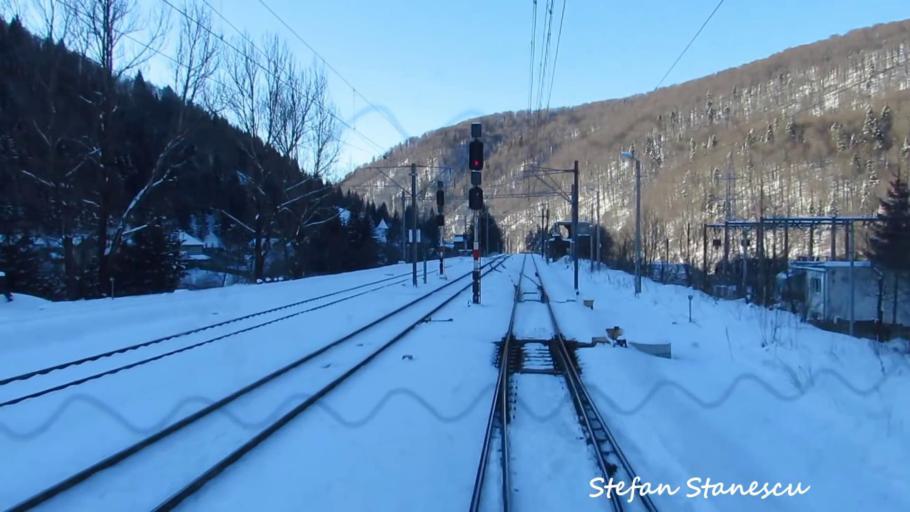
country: RO
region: Prahova
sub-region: Oras Azuga
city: Azuga
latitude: 45.4359
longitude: 25.5508
